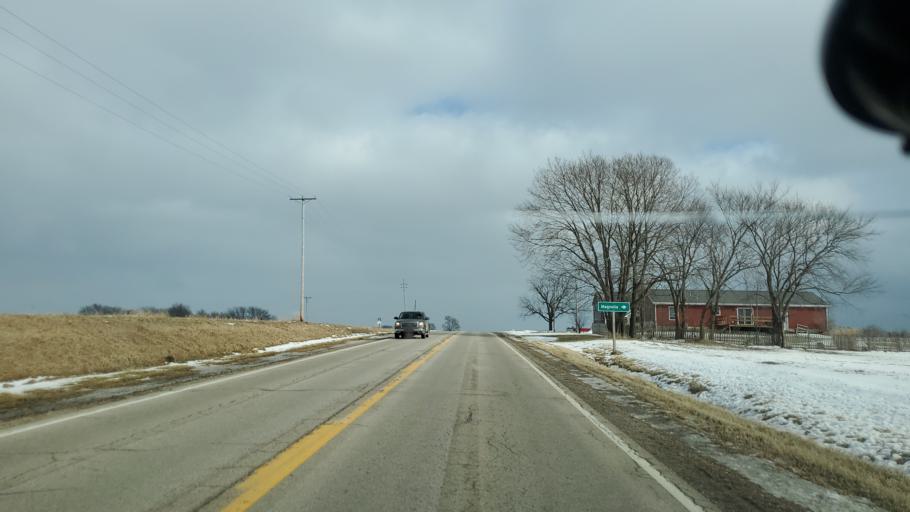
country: US
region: Illinois
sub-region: Marshall County
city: Toluca
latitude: 41.1185
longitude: -89.1961
